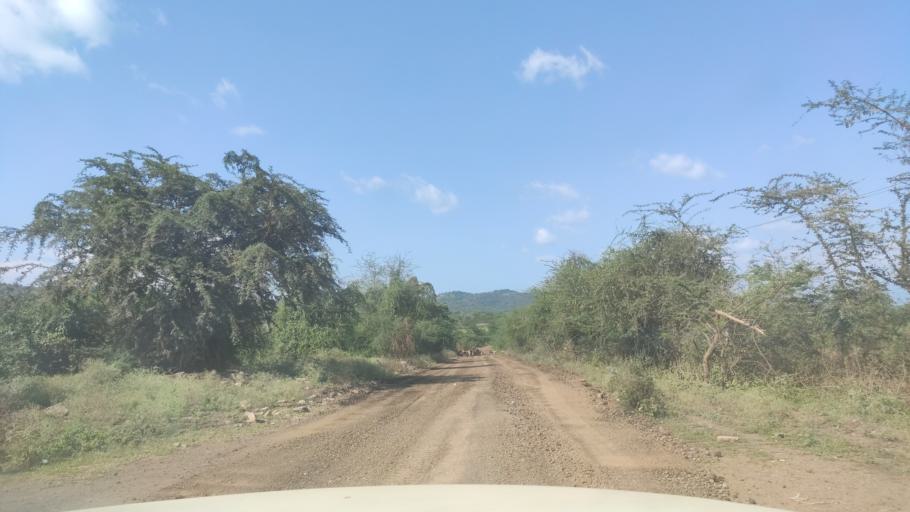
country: ET
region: Southern Nations, Nationalities, and People's Region
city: Felege Neway
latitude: 6.3745
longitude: 37.0872
